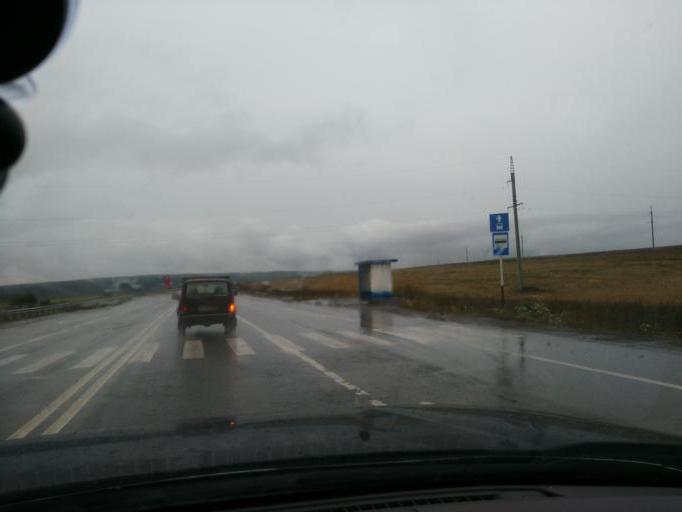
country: RU
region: Perm
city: Yugo-Kamskiy
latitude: 57.7012
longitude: 55.6237
